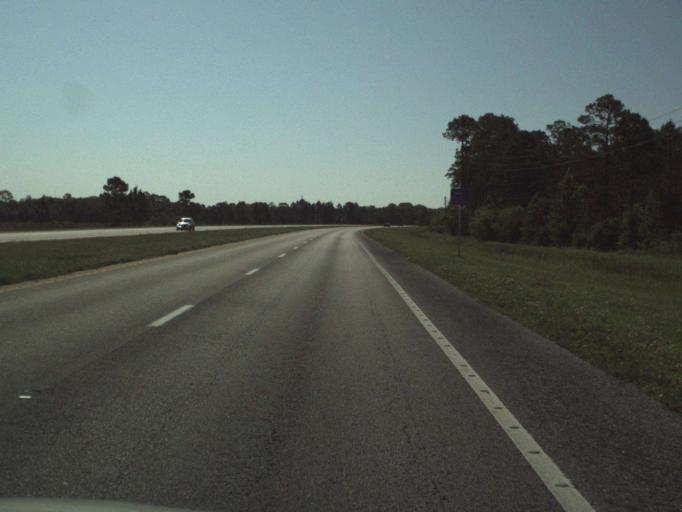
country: US
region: Florida
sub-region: Orange County
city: Christmas
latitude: 28.4660
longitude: -80.9985
